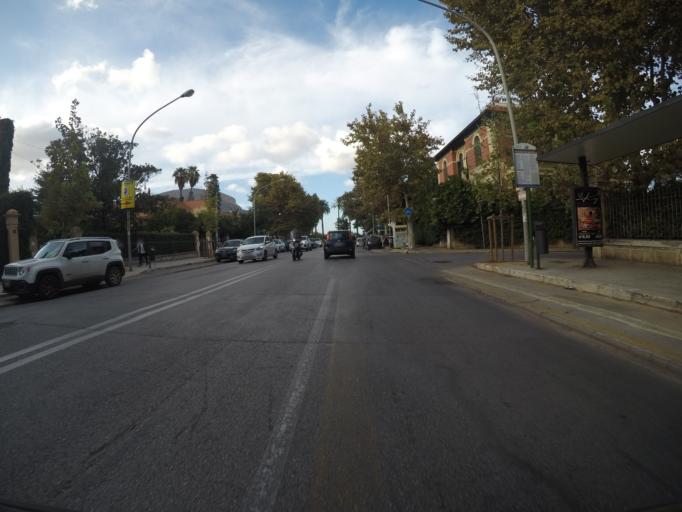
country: IT
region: Sicily
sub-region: Palermo
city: Palermo
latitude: 38.1959
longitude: 13.3320
